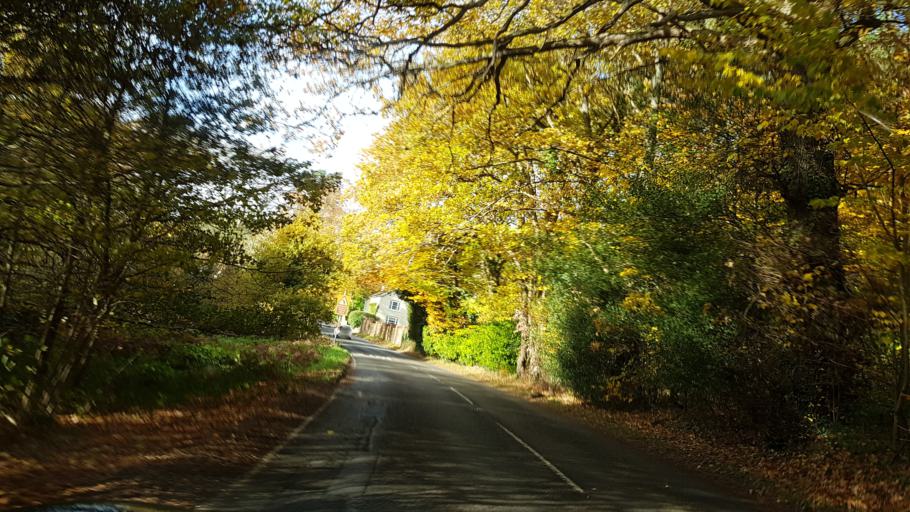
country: GB
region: England
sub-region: Surrey
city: Elstead
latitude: 51.1907
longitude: -0.7203
